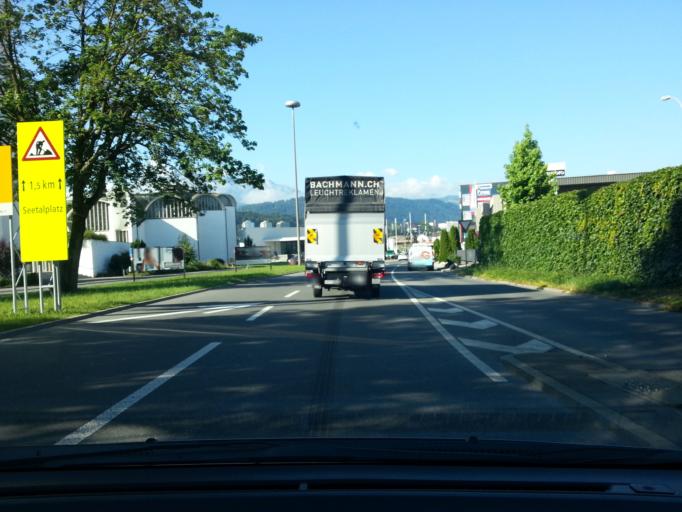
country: CH
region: Lucerne
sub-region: Hochdorf District
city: Emmen
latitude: 47.0718
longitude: 8.2857
